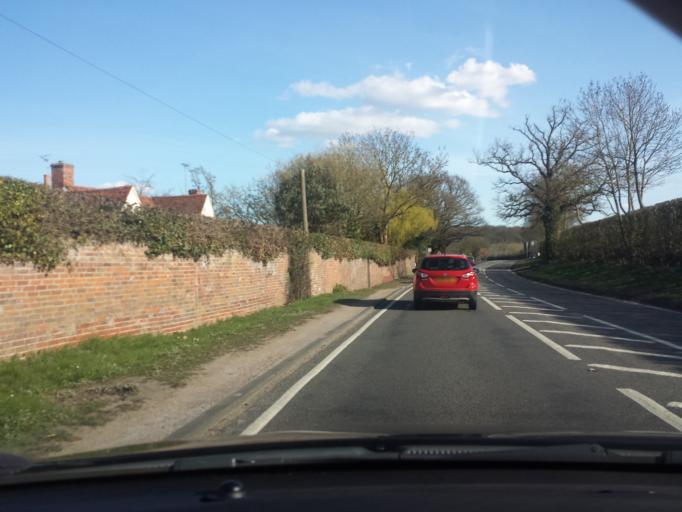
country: GB
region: England
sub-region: Essex
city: Alresford
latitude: 51.8495
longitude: 1.0140
